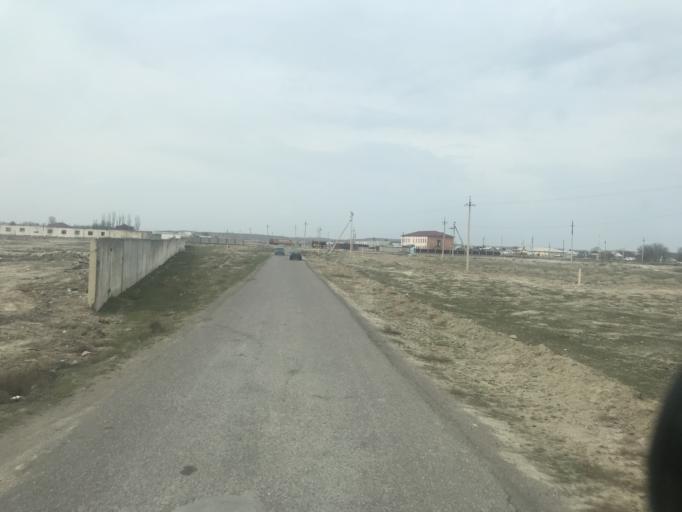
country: KZ
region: Ongtustik Qazaqstan
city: Shardara
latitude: 41.2623
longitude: 67.9456
